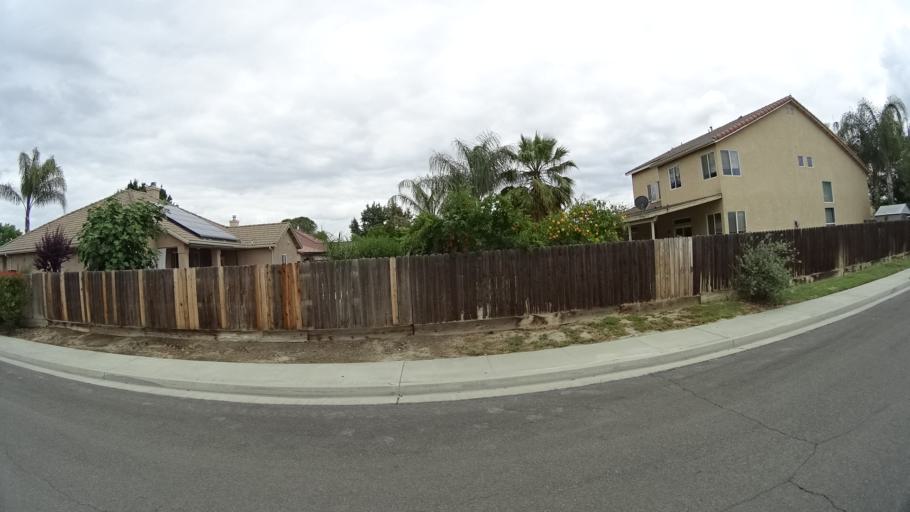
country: US
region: California
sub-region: Kings County
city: Armona
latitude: 36.3330
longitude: -119.6811
